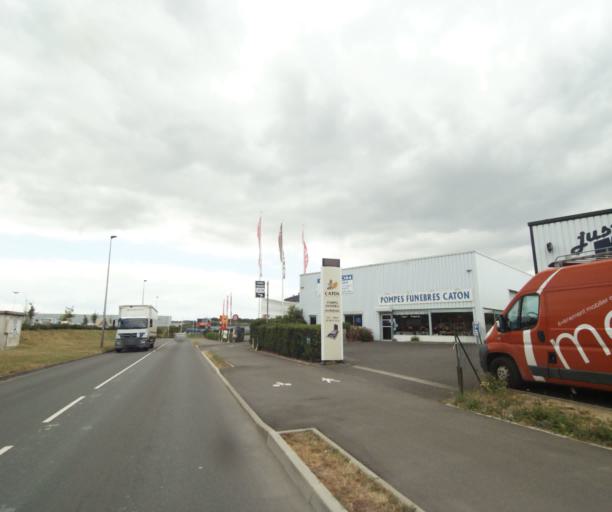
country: FR
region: Centre
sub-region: Departement du Loiret
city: Checy
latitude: 47.9051
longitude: 2.0363
